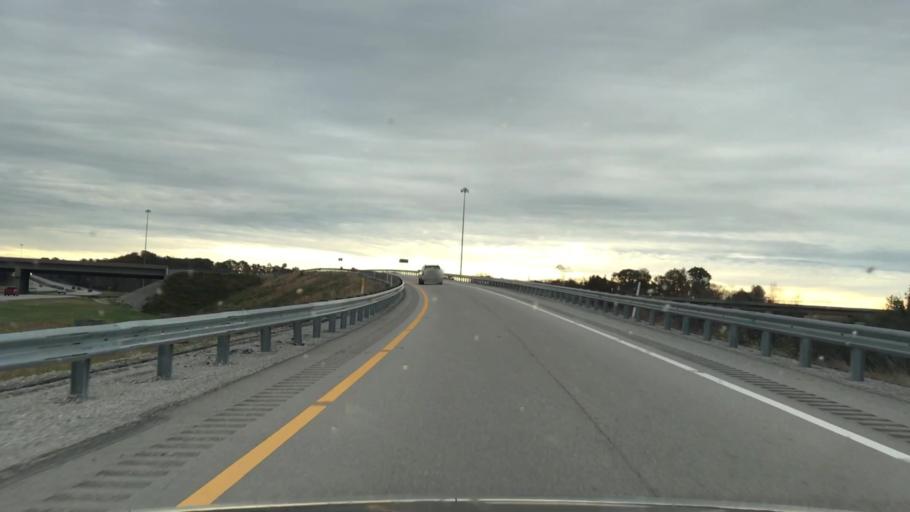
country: US
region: Kentucky
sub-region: Barren County
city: Glasgow
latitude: 36.9927
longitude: -85.9833
